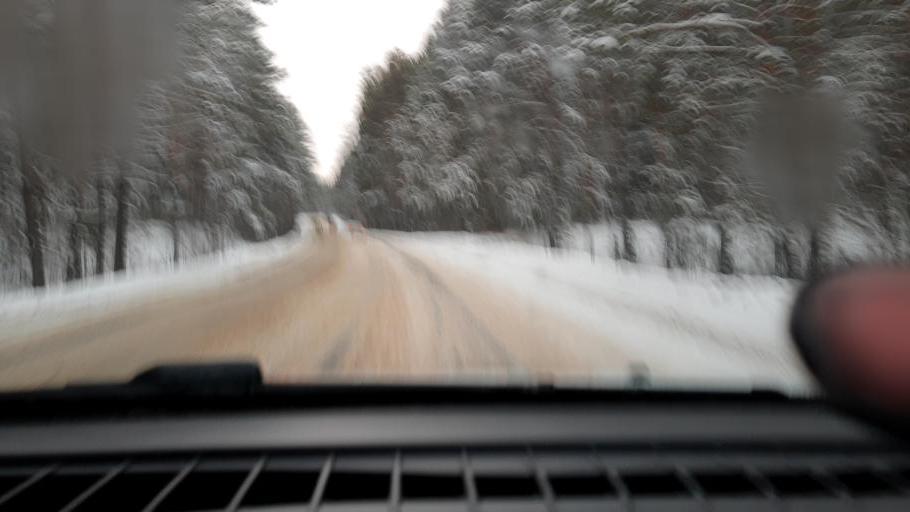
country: RU
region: Nizjnij Novgorod
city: Pamyat' Parizhskoy Kommuny
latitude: 56.2787
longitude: 44.3871
